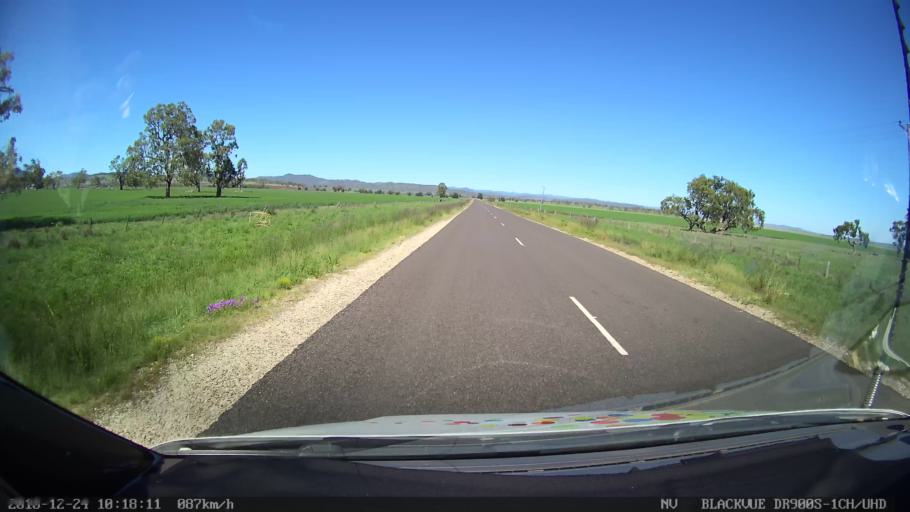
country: AU
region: New South Wales
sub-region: Liverpool Plains
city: Quirindi
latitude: -31.7228
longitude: 150.5800
